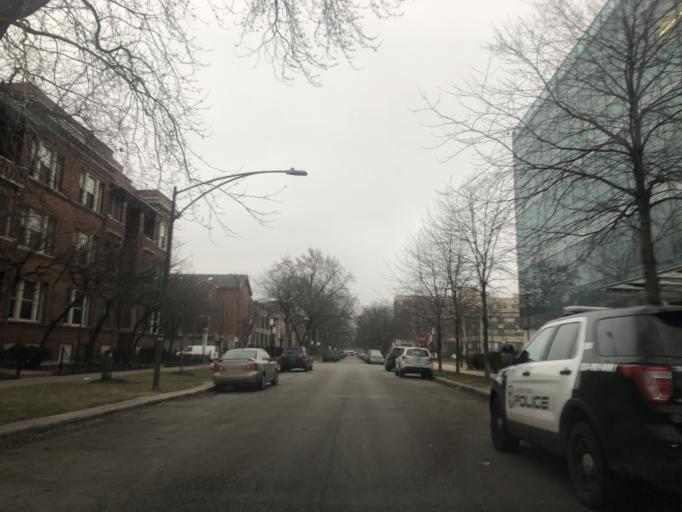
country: US
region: Illinois
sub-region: Cook County
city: Chicago
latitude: 41.7846
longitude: -87.6043
